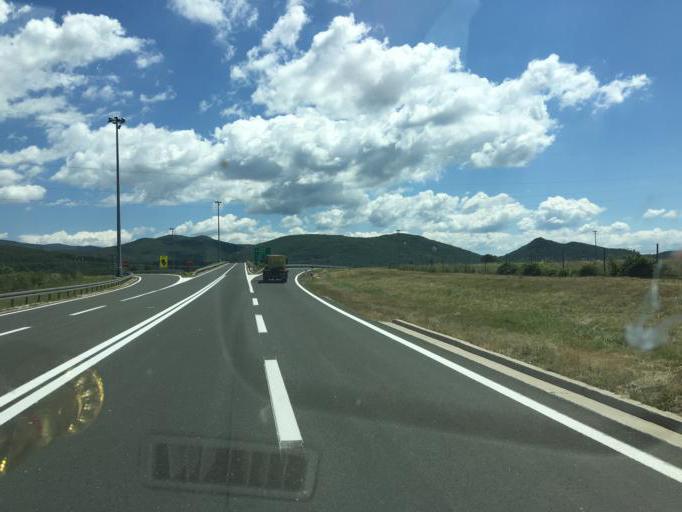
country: HR
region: Licko-Senjska
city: Gospic
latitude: 44.5735
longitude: 15.4230
